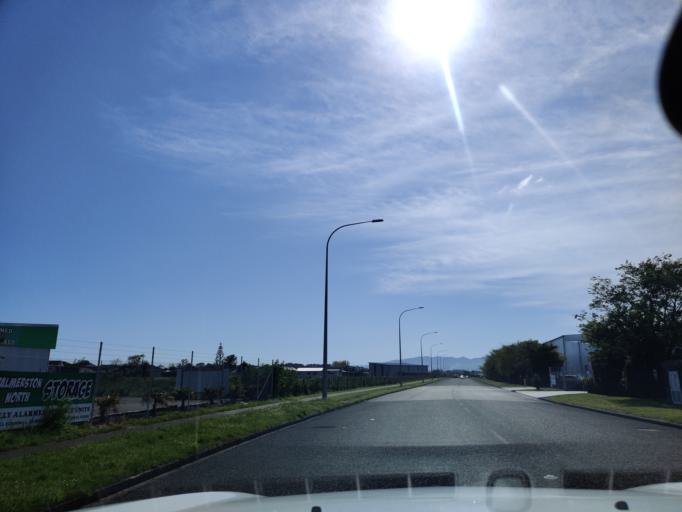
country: NZ
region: Manawatu-Wanganui
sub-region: Palmerston North City
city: Palmerston North
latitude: -40.3335
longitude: 175.6458
